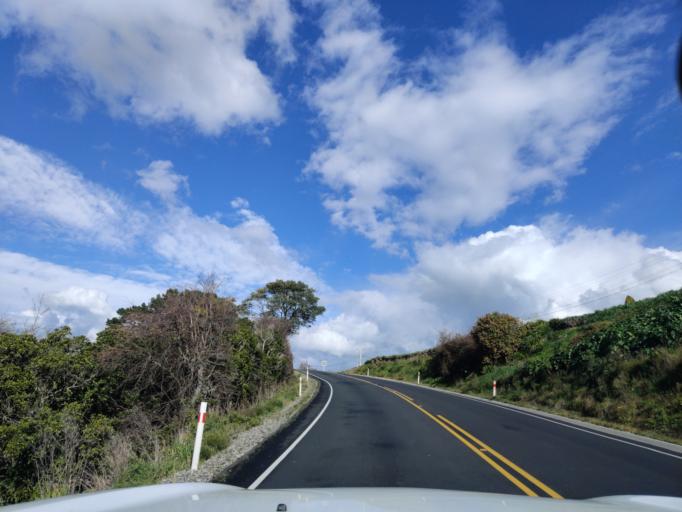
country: NZ
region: Manawatu-Wanganui
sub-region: Palmerston North City
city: Palmerston North
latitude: -40.2804
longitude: 175.7606
